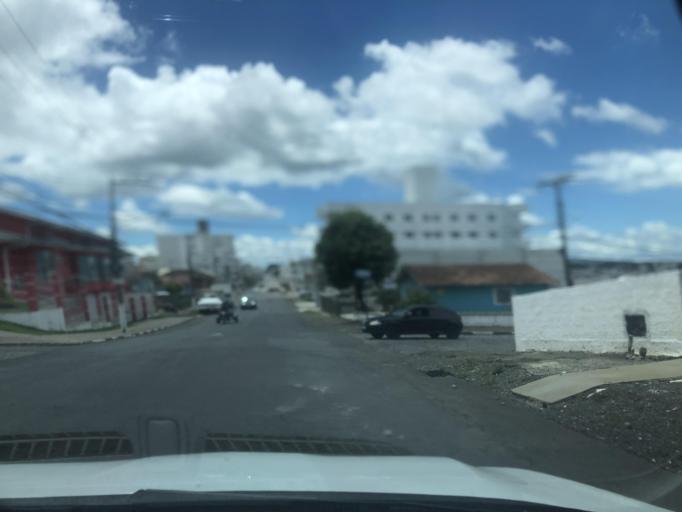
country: BR
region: Santa Catarina
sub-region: Lages
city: Lages
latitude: -27.8090
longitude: -50.3019
